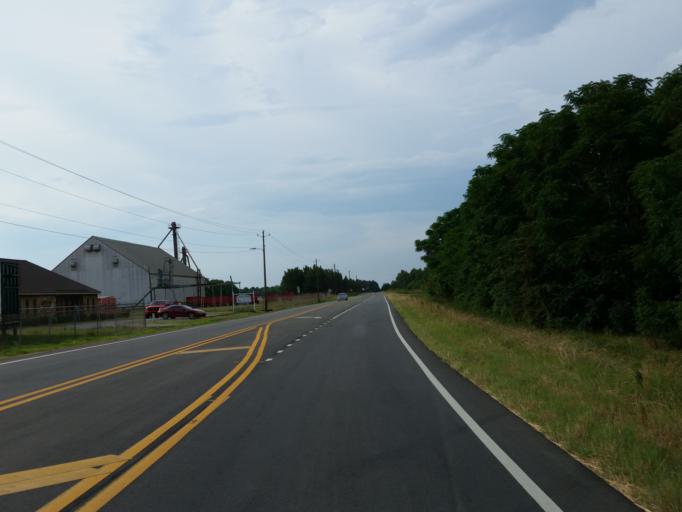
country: US
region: Georgia
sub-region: Turner County
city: Ashburn
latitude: 31.7224
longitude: -83.6645
